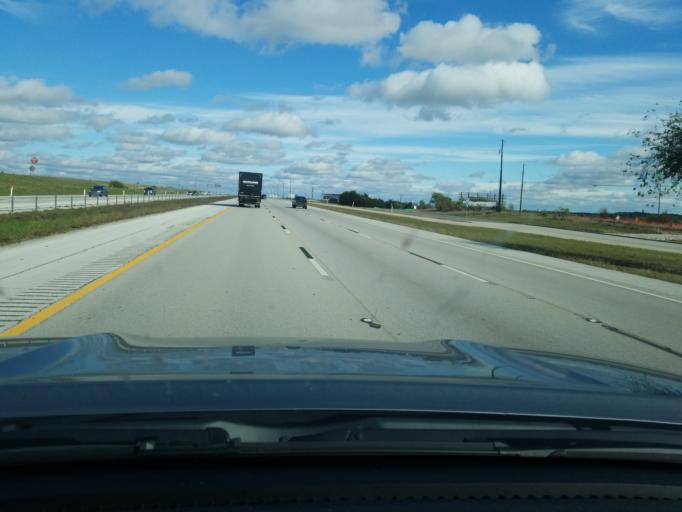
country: US
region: Texas
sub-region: Parker County
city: Aledo
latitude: 32.7211
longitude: -97.5540
